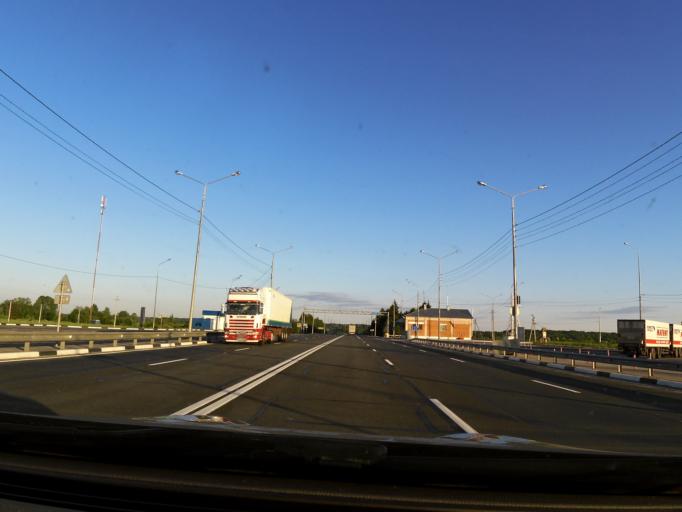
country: RU
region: Vologda
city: Gryazovets
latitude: 58.7434
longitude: 40.2879
